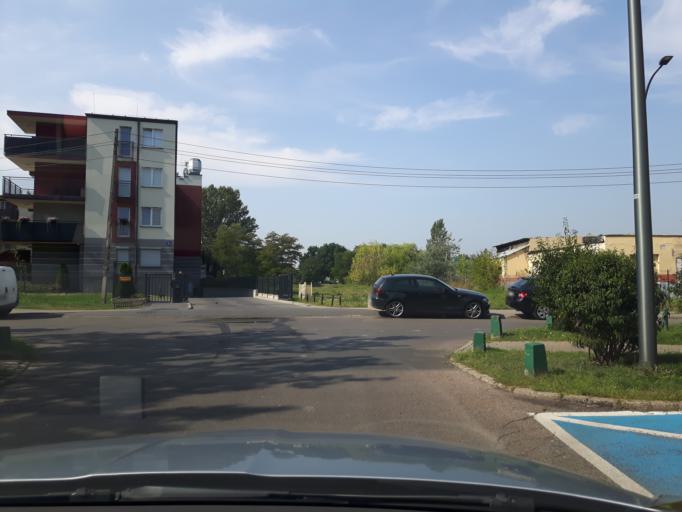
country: PL
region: Masovian Voivodeship
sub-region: Warszawa
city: Targowek
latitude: 52.3019
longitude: 21.0453
